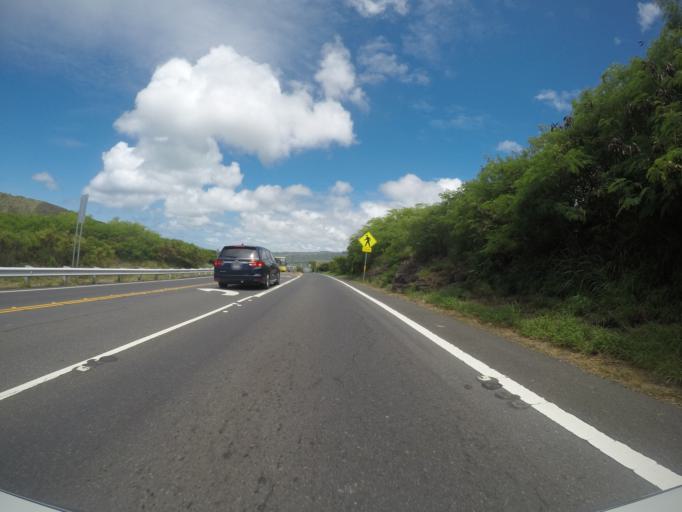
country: US
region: Hawaii
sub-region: Honolulu County
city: Waimanalo Beach
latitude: 21.2751
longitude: -157.6925
